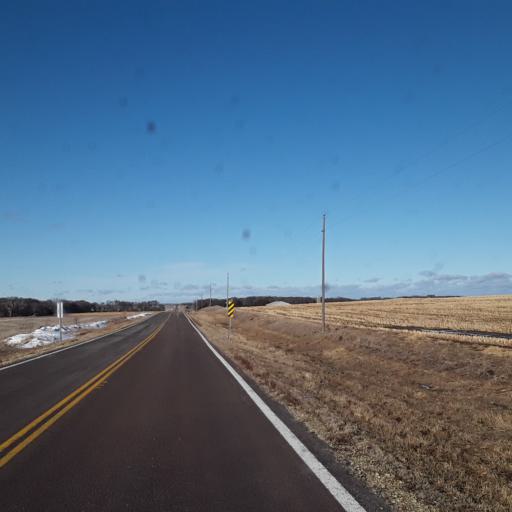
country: US
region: Kansas
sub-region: Cloud County
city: Concordia
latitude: 39.5328
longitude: -97.7228
